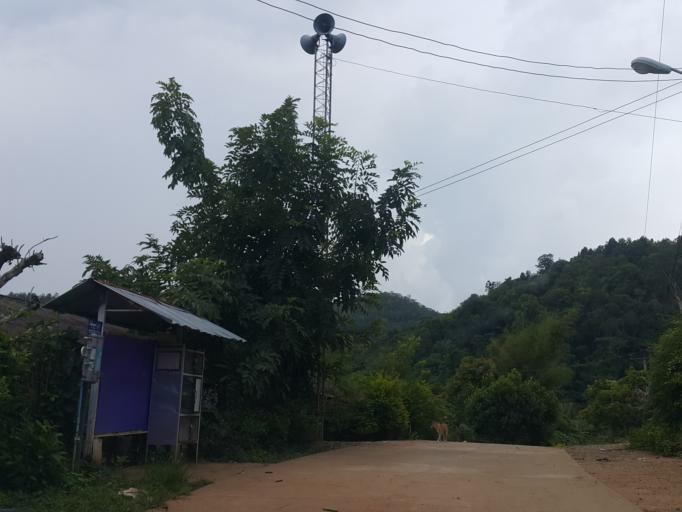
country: TH
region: Chiang Mai
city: Phrao
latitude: 19.3189
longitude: 99.1298
